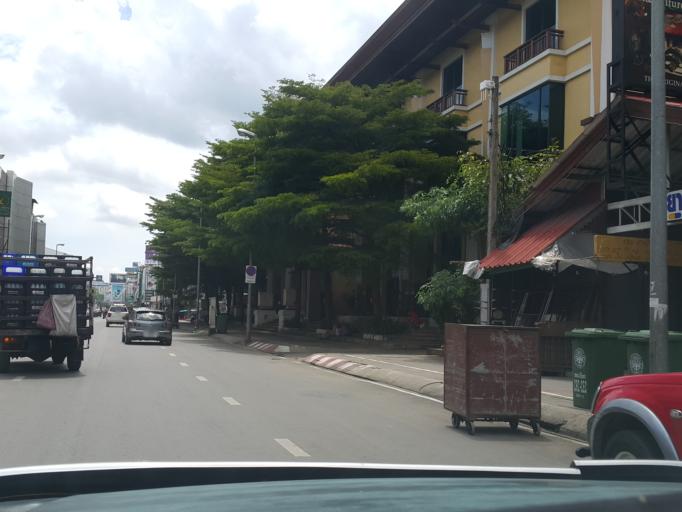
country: TH
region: Chiang Mai
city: Chiang Mai
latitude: 18.7850
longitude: 99.0005
